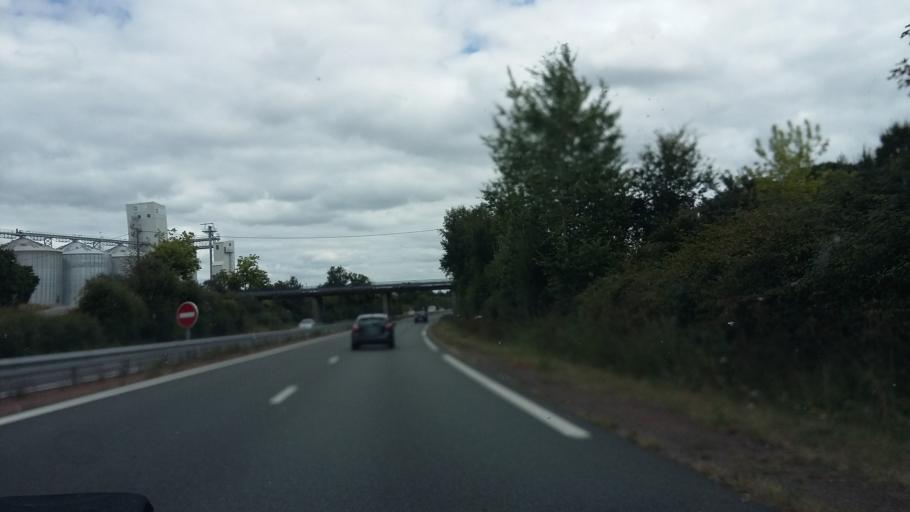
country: FR
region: Pays de la Loire
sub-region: Departement de la Vendee
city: La Genetouze
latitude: 46.7094
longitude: -1.5202
